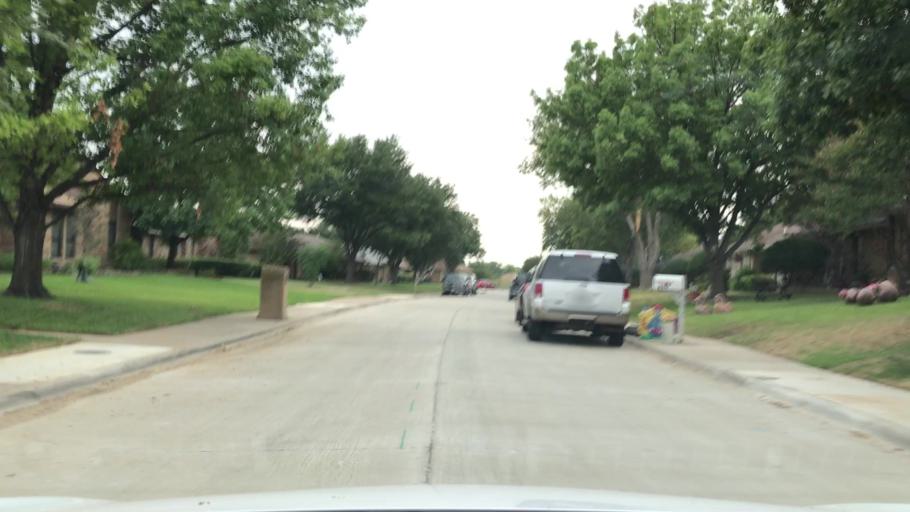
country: US
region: Texas
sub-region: Dallas County
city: Carrollton
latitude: 32.9922
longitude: -96.8720
